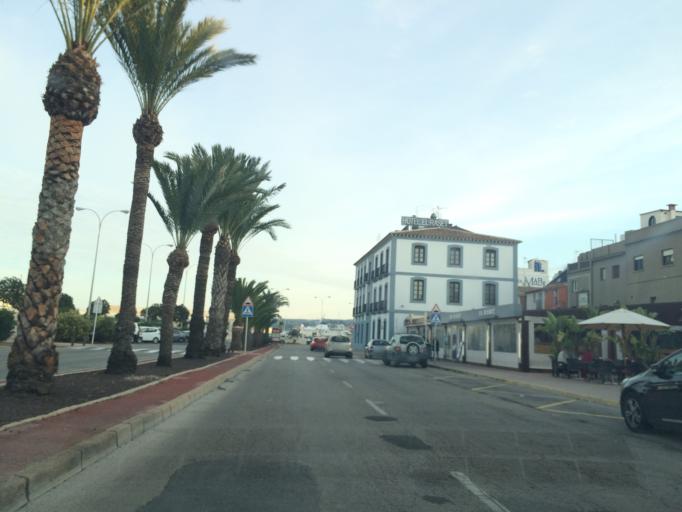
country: ES
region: Valencia
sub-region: Provincia de Alicante
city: Denia
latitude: 38.8449
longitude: 0.1098
